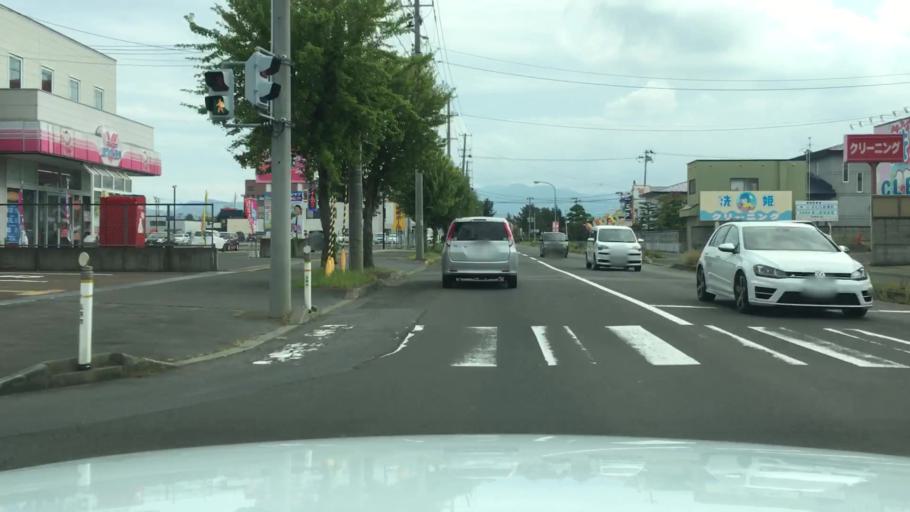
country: JP
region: Aomori
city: Hirosaki
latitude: 40.6194
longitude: 140.4845
